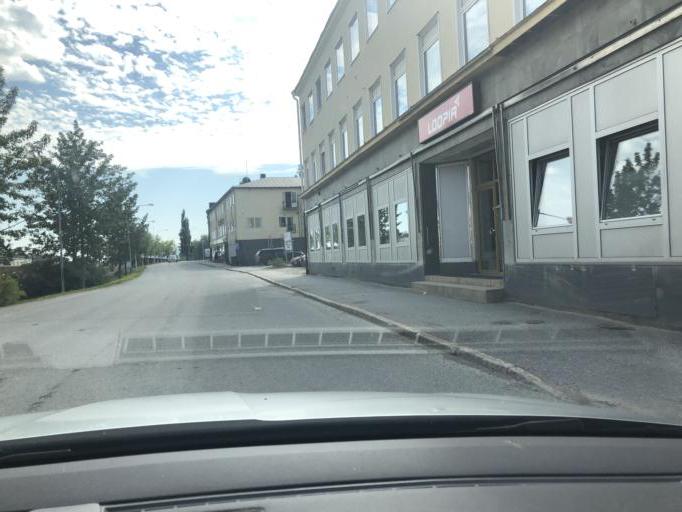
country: SE
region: Vaesternorrland
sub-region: Kramfors Kommun
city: Kramfors
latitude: 62.9298
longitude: 17.7763
